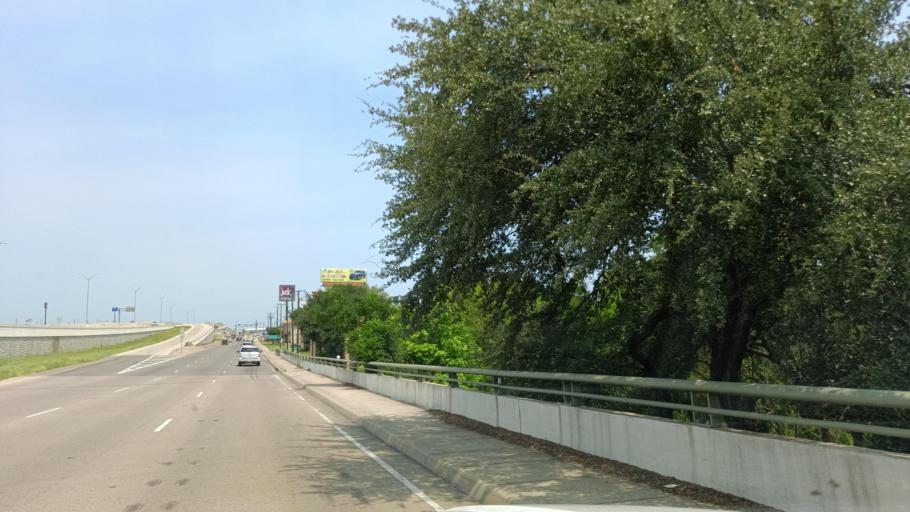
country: US
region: Texas
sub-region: Bell County
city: Temple
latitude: 31.0864
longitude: -97.3848
